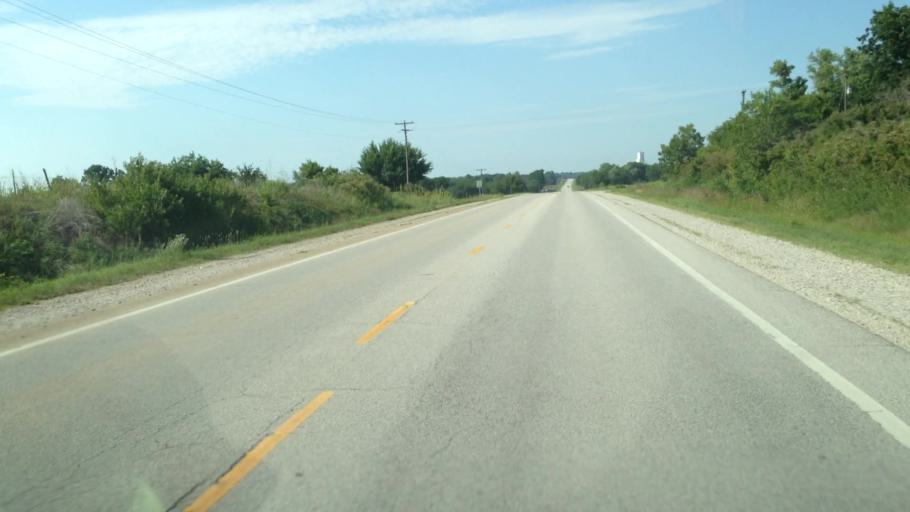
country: US
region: Kansas
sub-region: Neosho County
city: Erie
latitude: 37.4990
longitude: -95.2696
